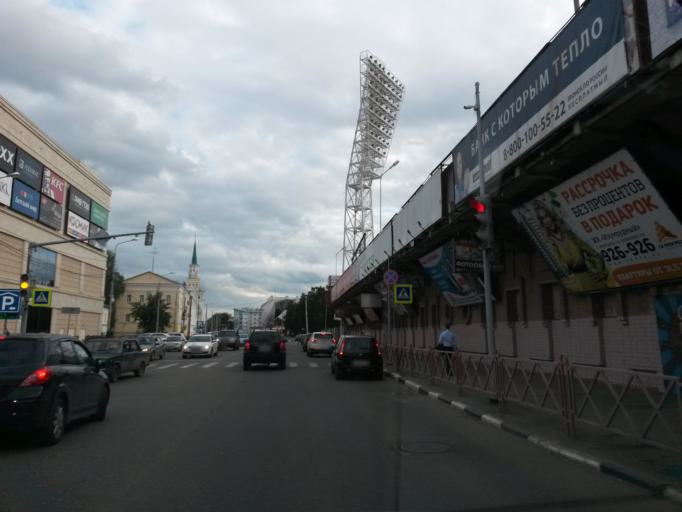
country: RU
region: Jaroslavl
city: Yaroslavl
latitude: 57.6286
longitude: 39.8687
